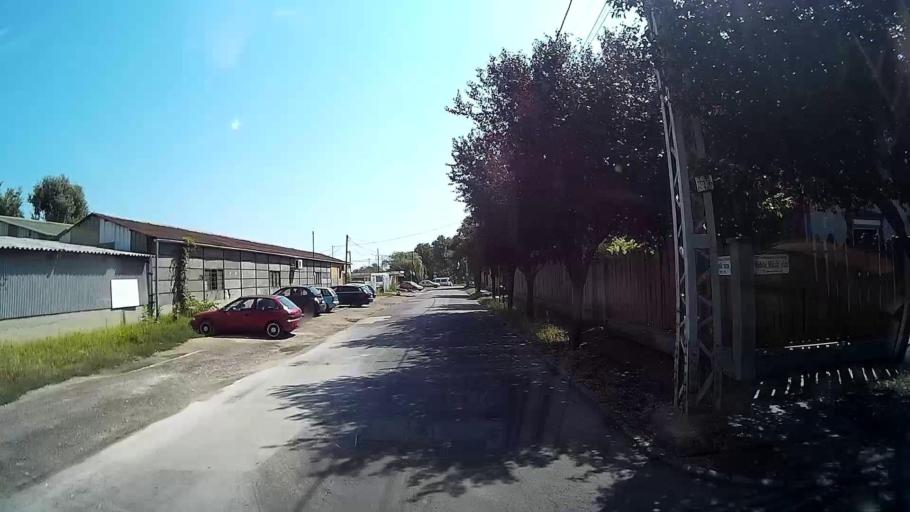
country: HU
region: Budapest
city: Budapest XVIII. keruelet
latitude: 47.4523
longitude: 19.1937
